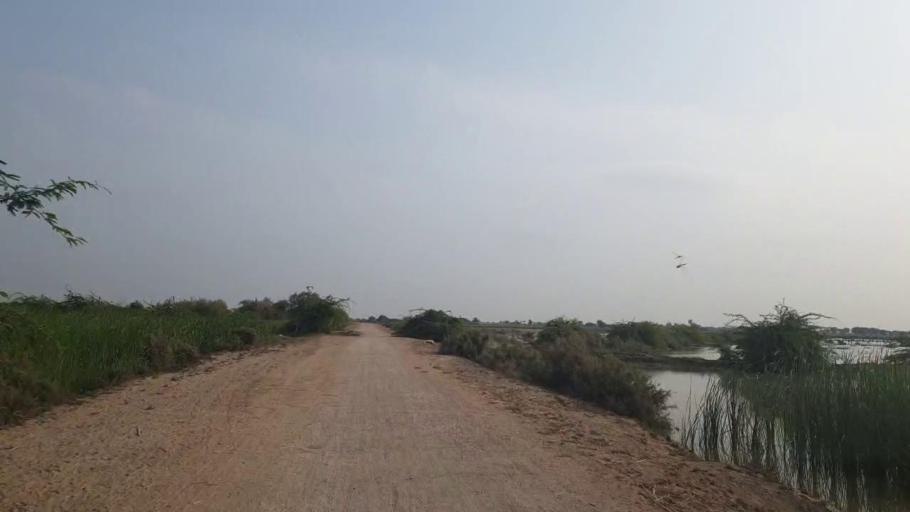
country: PK
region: Sindh
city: Badin
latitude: 24.6028
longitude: 68.6956
